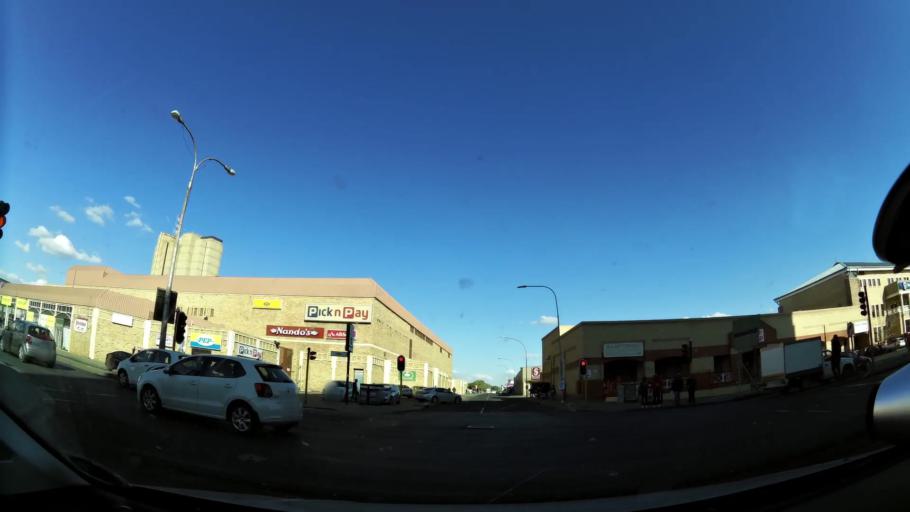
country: ZA
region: Northern Cape
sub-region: Frances Baard District Municipality
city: Kimberley
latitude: -28.7431
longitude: 24.7638
